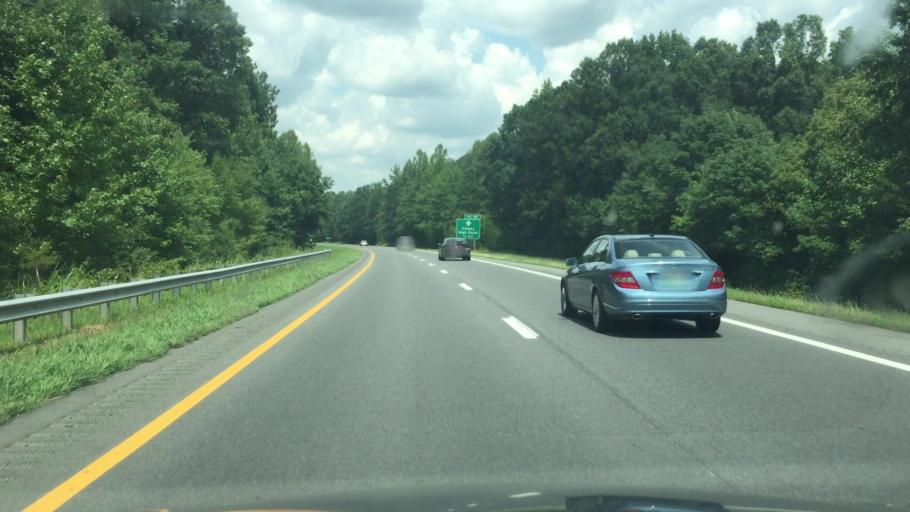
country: US
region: North Carolina
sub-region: Guilford County
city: Pleasant Garden
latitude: 35.9072
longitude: -79.8216
